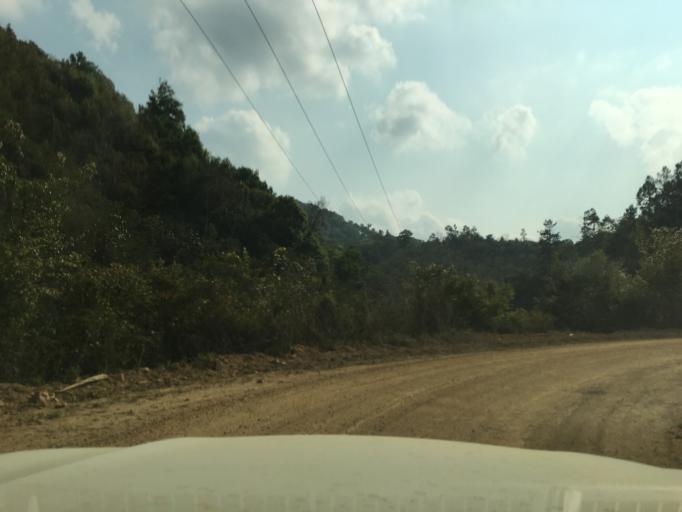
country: LA
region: Houaphan
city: Huameung
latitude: 20.2065
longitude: 103.8540
